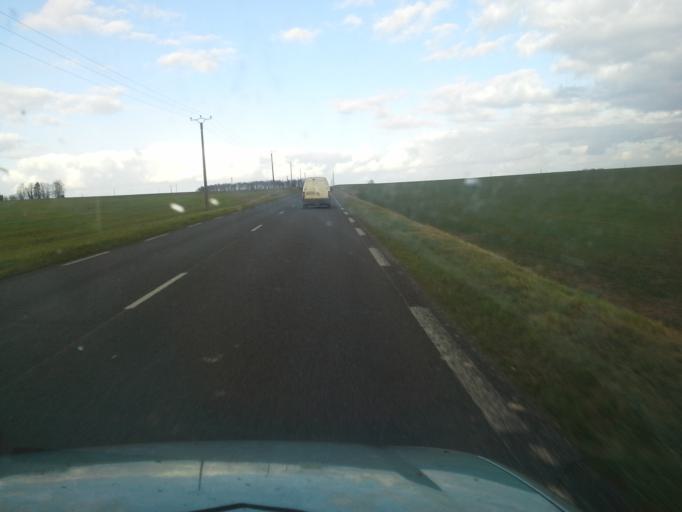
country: FR
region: Centre
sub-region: Departement d'Indre-et-Loire
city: Monnaie
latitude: 47.5182
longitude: 0.8165
